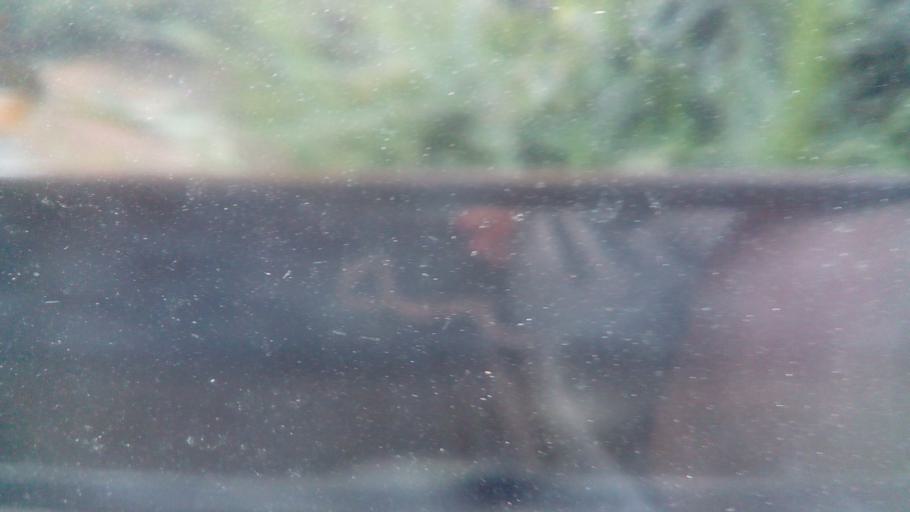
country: TW
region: Taiwan
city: Daxi
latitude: 24.4636
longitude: 121.3938
